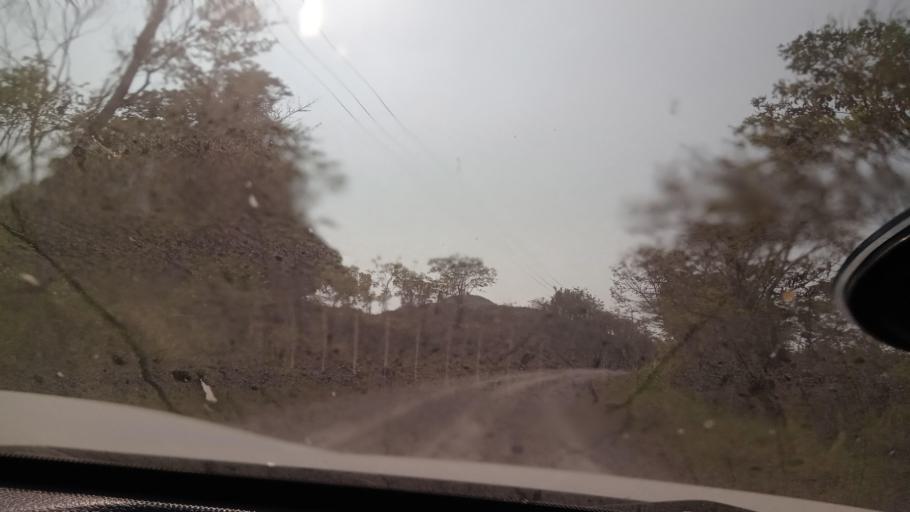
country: MX
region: Tabasco
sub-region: Huimanguillo
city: Francisco Rueda
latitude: 17.6121
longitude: -93.9365
